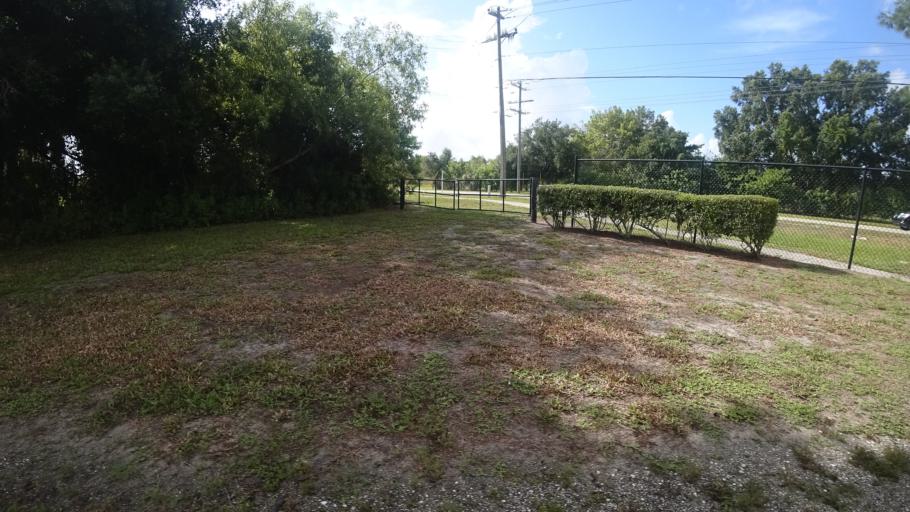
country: US
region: Florida
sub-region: Manatee County
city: Ellenton
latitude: 27.5743
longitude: -82.4843
